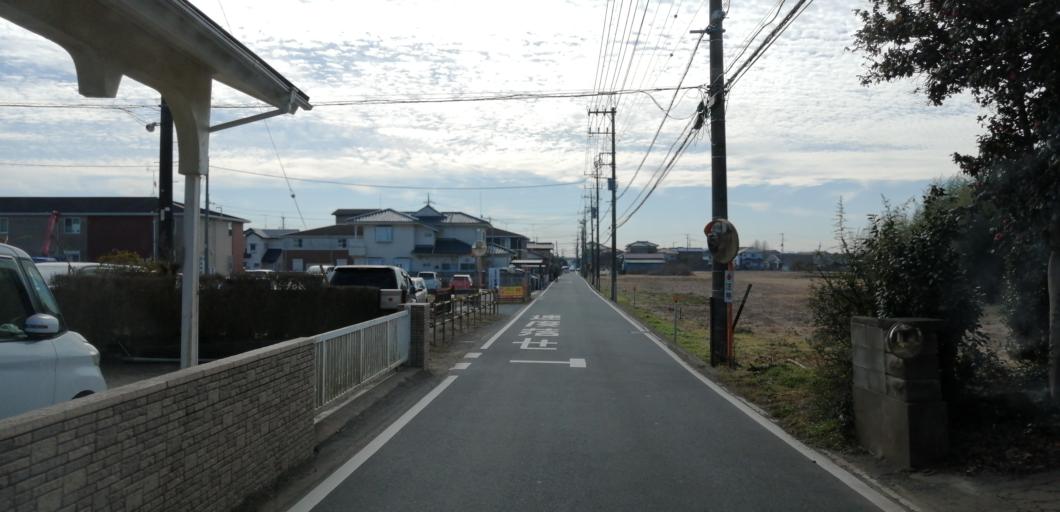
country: JP
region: Chiba
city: Narita
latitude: 35.7440
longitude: 140.3320
